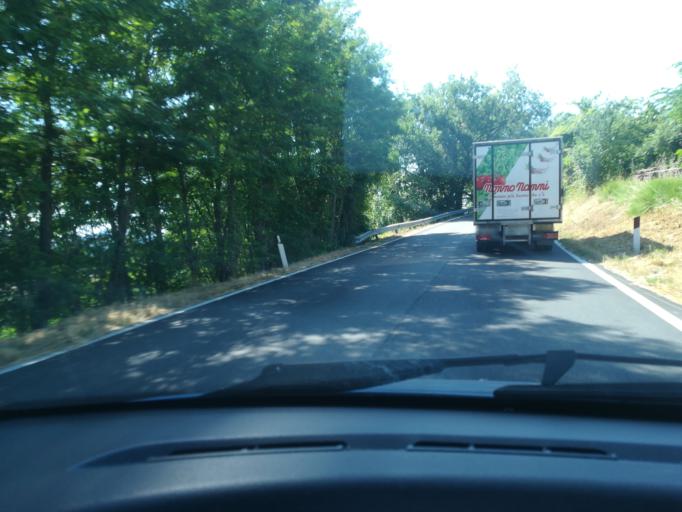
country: IT
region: The Marches
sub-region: Provincia di Macerata
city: Ripe San Ginesio
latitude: 43.1110
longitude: 13.3613
